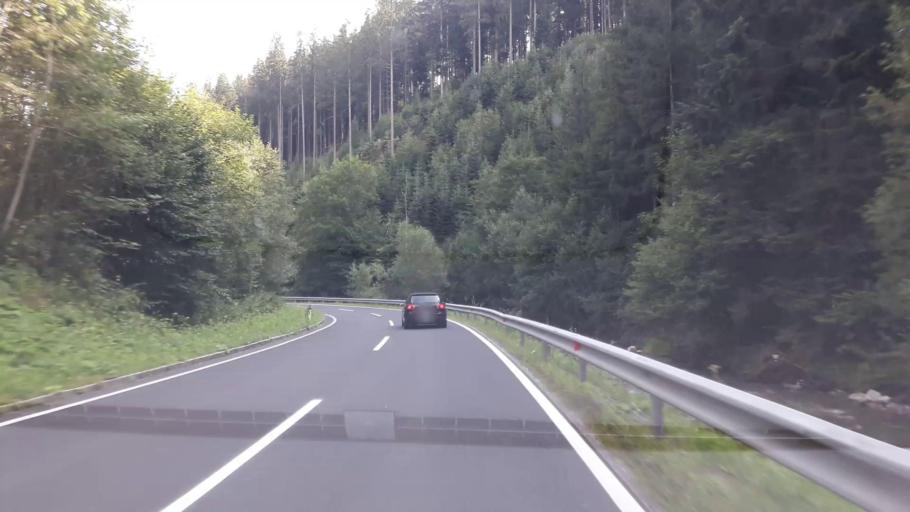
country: AT
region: Styria
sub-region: Politischer Bezirk Weiz
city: Birkfeld
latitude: 47.3347
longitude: 15.6882
